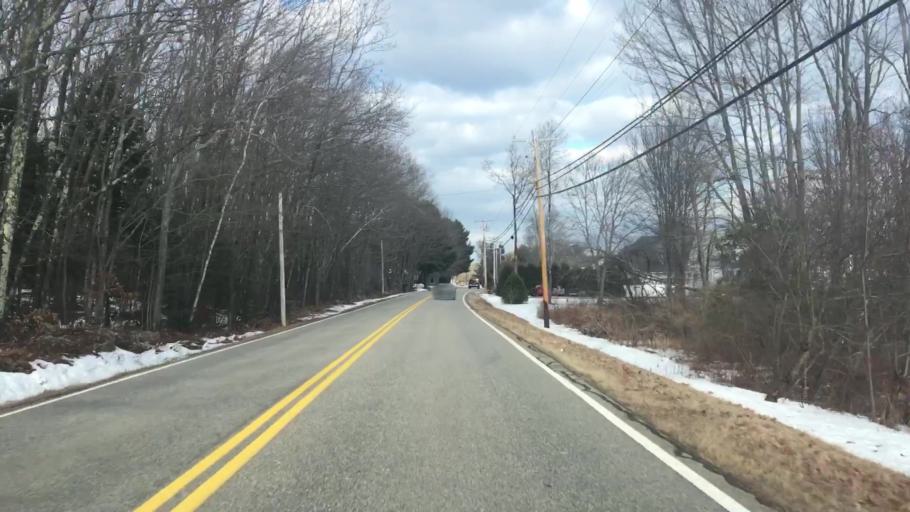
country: US
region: Maine
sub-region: York County
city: Biddeford
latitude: 43.4529
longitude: -70.4322
